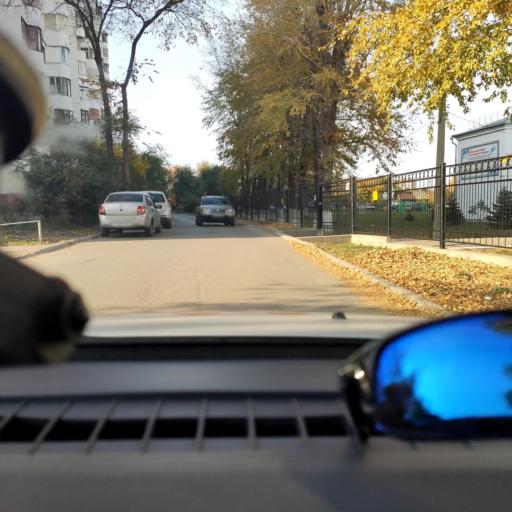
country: RU
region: Samara
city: Samara
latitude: 53.2284
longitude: 50.2318
